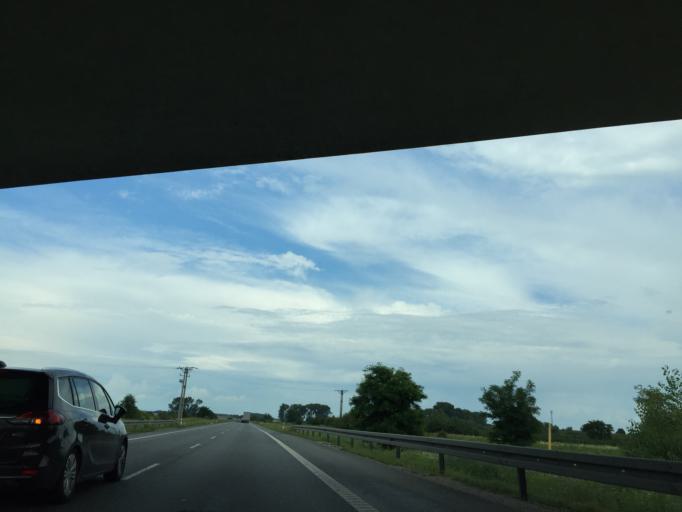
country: PL
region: Masovian Voivodeship
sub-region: Powiat grojecki
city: Chynow
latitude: 51.8993
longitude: 21.0142
